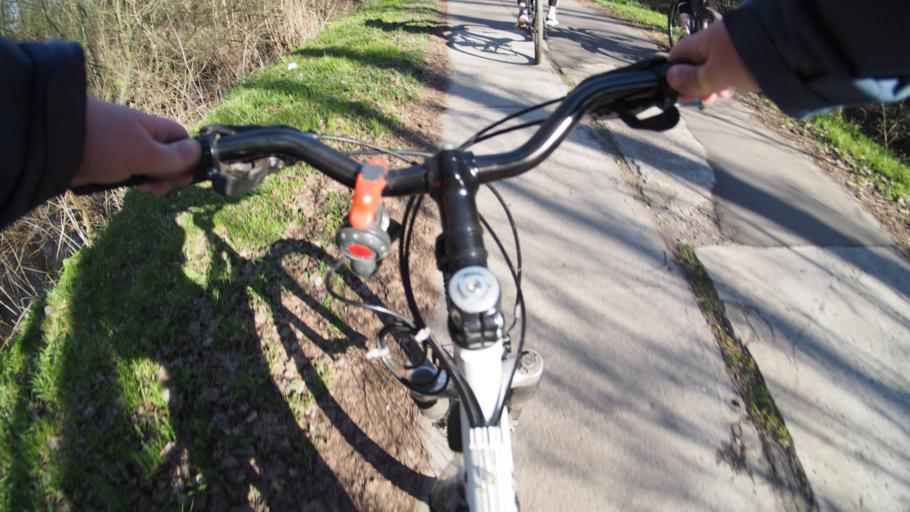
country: RU
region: Moskovskaya
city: Malyshevo
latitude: 55.5218
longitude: 38.3239
